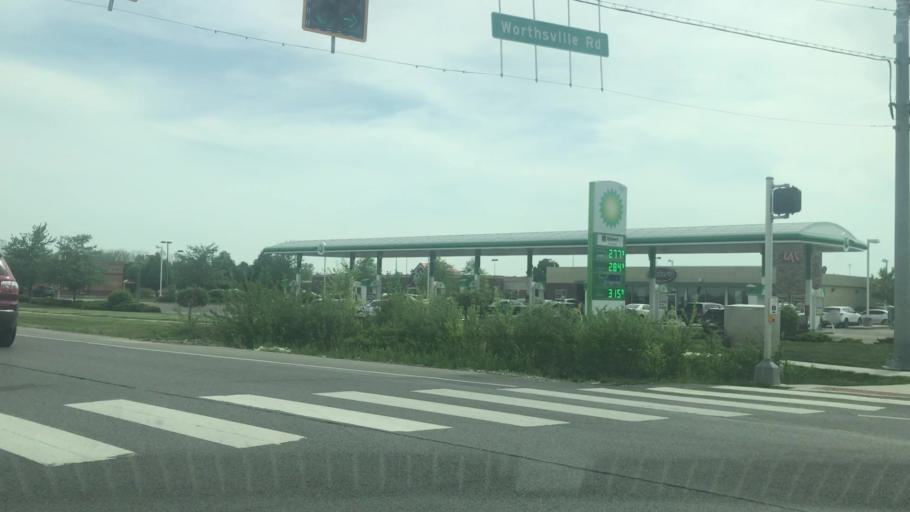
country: US
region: Indiana
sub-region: Johnson County
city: Greenwood
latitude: 39.5865
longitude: -86.1008
